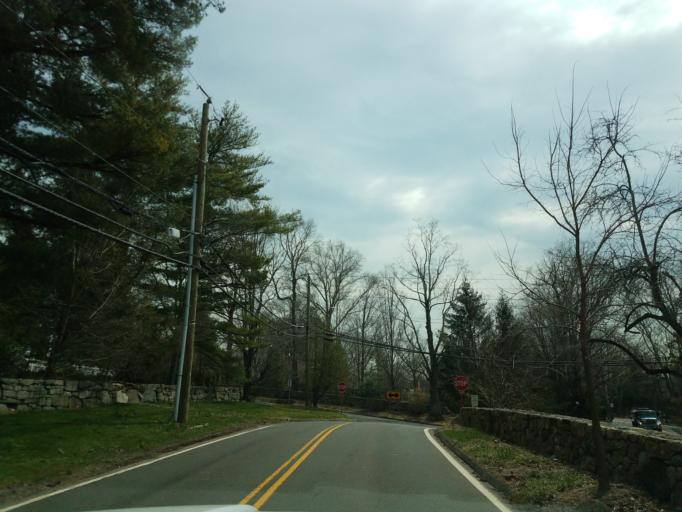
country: US
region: Connecticut
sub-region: Fairfield County
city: Glenville
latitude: 41.0912
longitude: -73.6477
